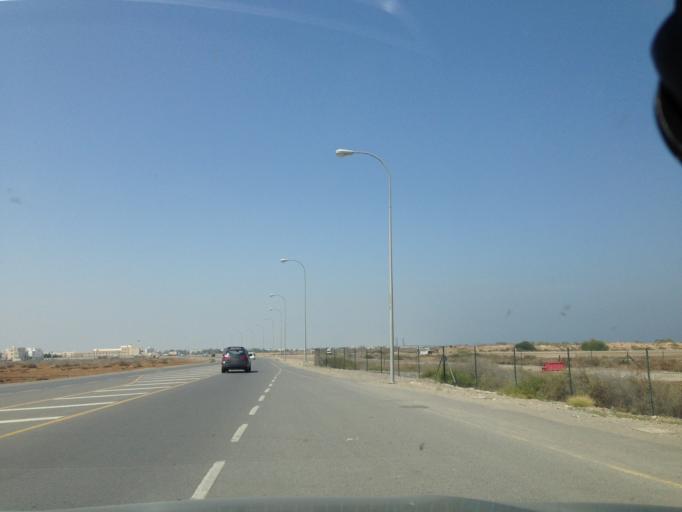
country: OM
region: Muhafazat Masqat
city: As Sib al Jadidah
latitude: 23.6274
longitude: 58.2600
